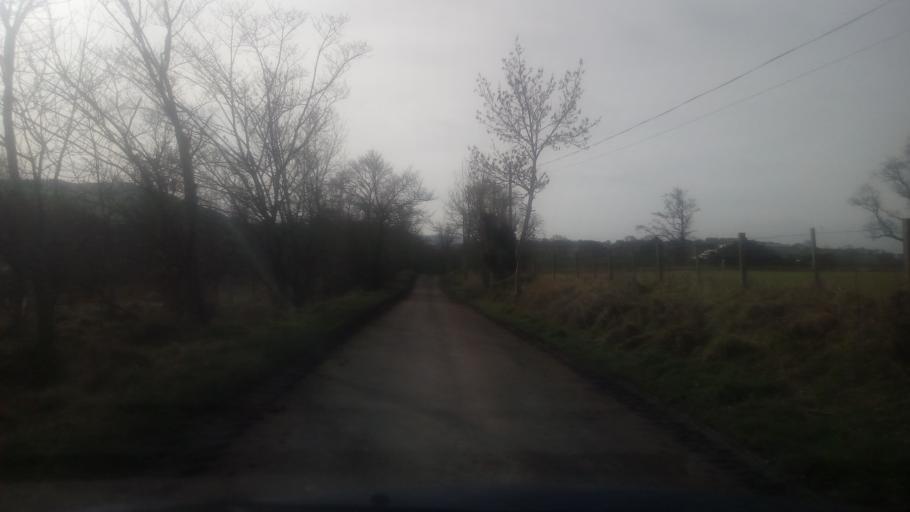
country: GB
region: Scotland
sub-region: The Scottish Borders
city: Jedburgh
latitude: 55.4216
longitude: -2.6437
